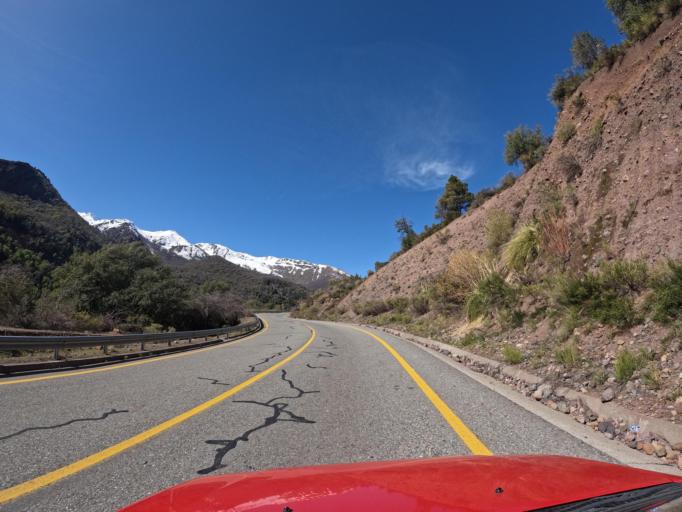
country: CL
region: Maule
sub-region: Provincia de Linares
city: Colbun
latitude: -35.8199
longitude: -70.7795
